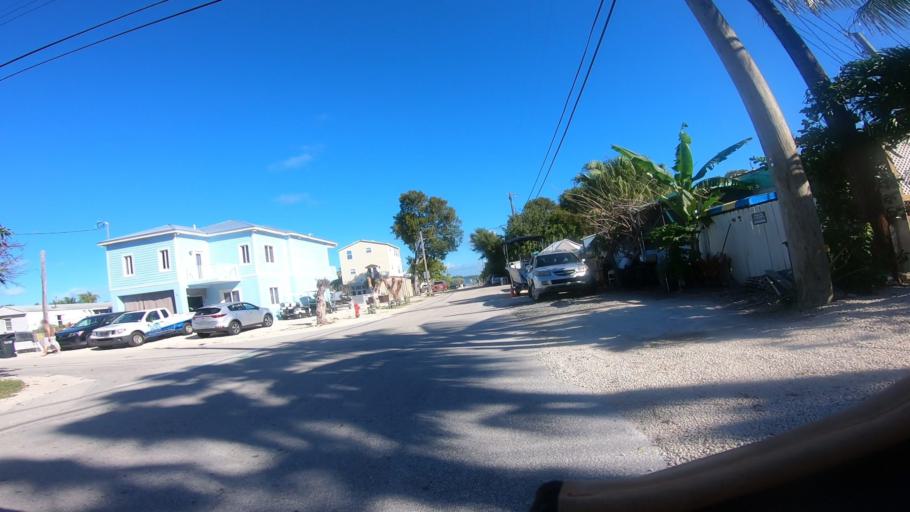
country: US
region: Florida
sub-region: Monroe County
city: Key Largo
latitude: 25.1138
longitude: -80.4257
